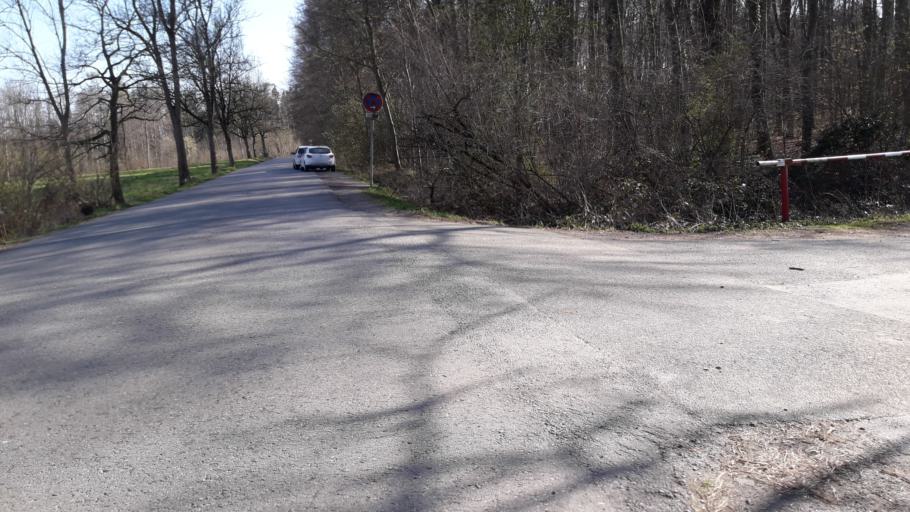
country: DE
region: North Rhine-Westphalia
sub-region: Regierungsbezirk Detmold
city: Paderborn
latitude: 51.6798
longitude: 8.6873
